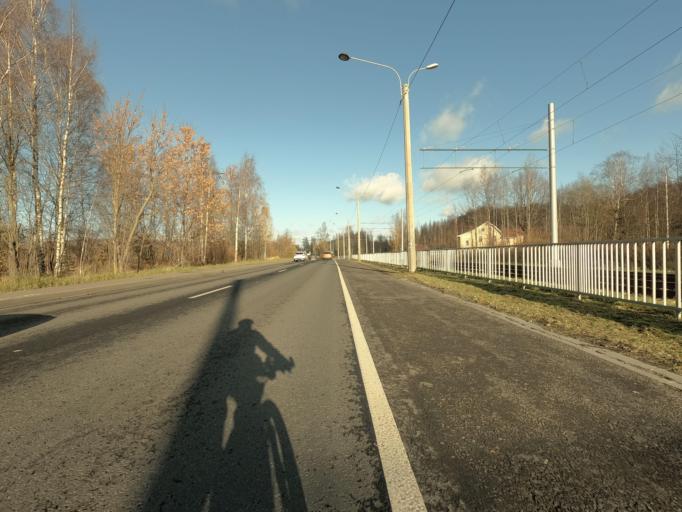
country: RU
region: St.-Petersburg
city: Krasnogvargeisky
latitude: 59.9667
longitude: 30.5019
